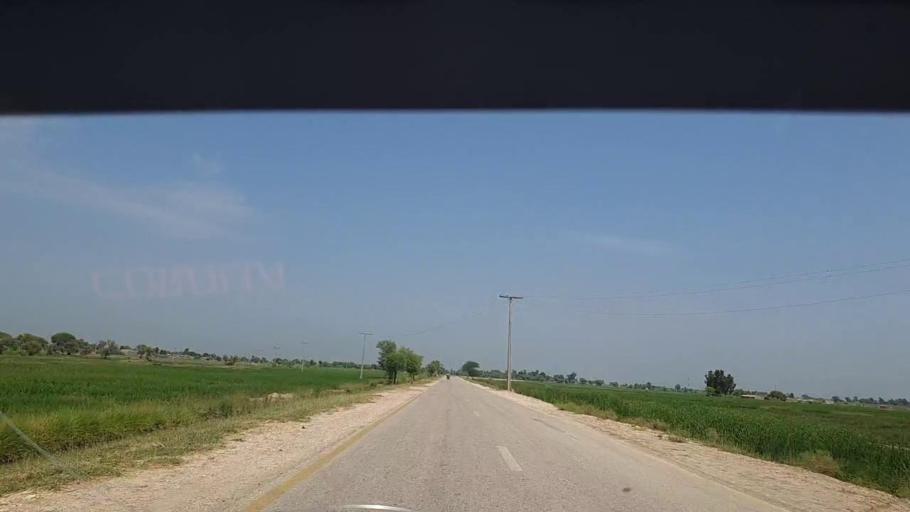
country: PK
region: Sindh
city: Rustam jo Goth
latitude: 28.1023
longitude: 68.8033
